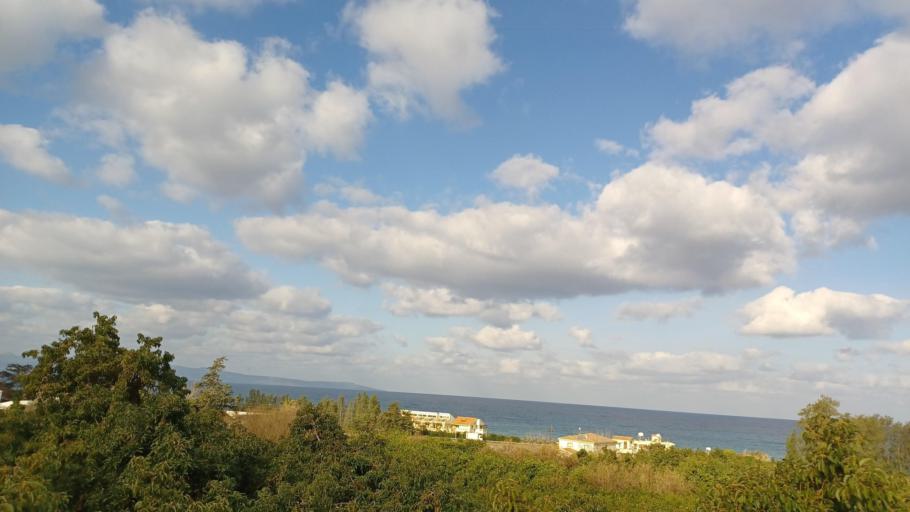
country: CY
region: Pafos
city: Polis
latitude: 35.1255
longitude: 32.5186
